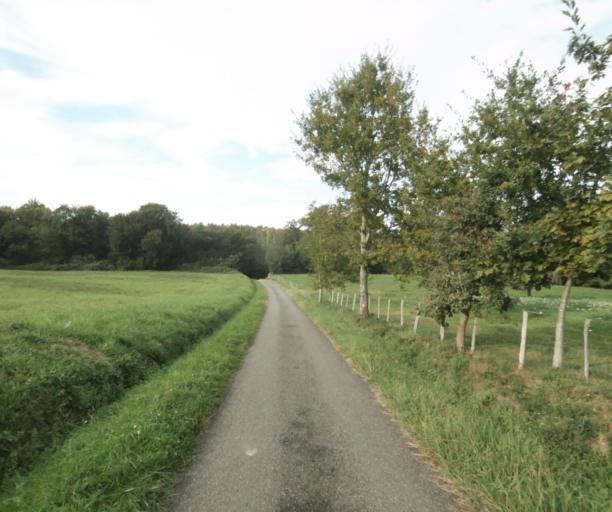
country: FR
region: Midi-Pyrenees
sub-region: Departement du Gers
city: Cazaubon
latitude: 43.8723
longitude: -0.1172
